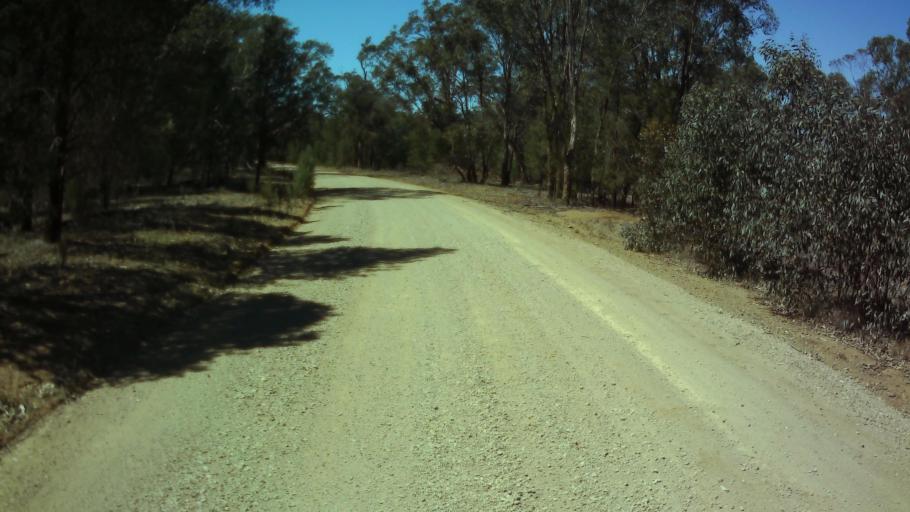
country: AU
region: New South Wales
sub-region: Weddin
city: Grenfell
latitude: -33.8583
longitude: 148.0868
